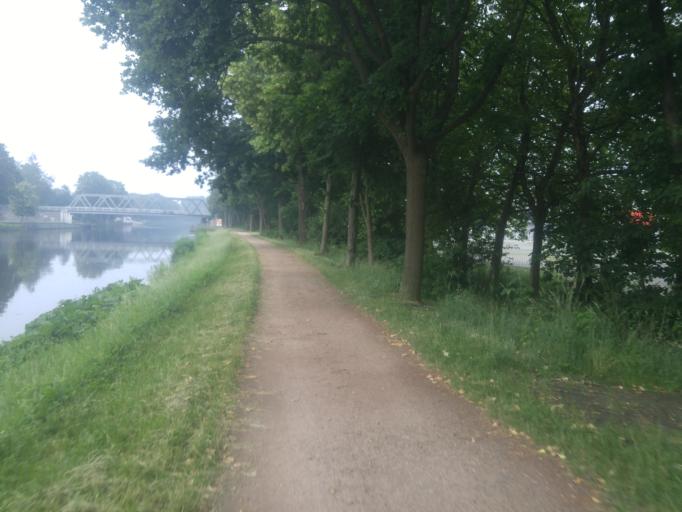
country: DE
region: Lower Saxony
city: Lingen
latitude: 52.5120
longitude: 7.3132
